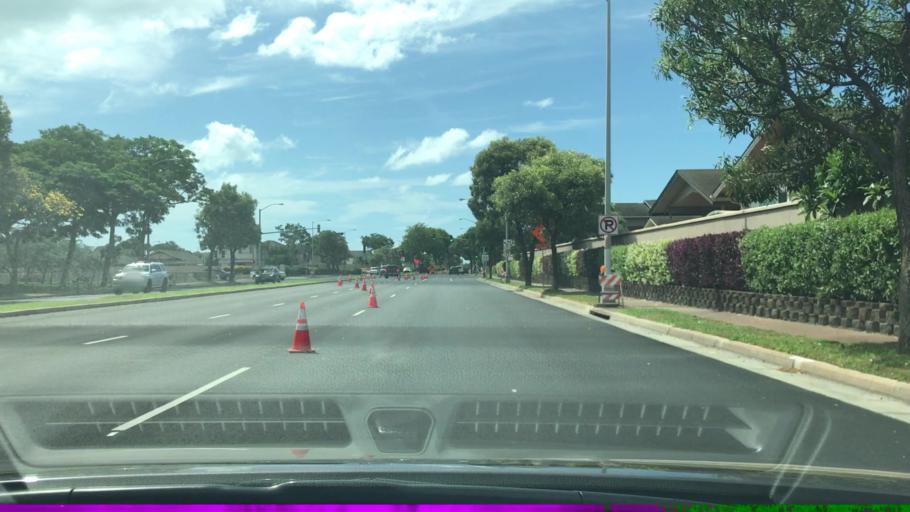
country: US
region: Hawaii
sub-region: Honolulu County
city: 'Ewa Gentry
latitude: 21.3330
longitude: -158.0287
